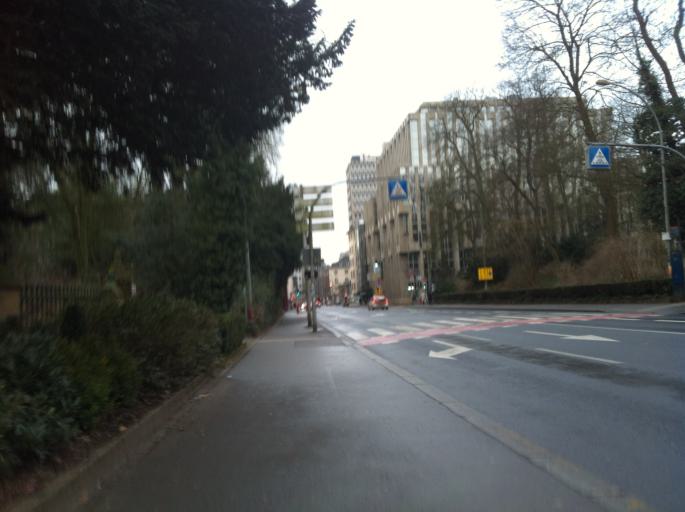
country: LU
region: Luxembourg
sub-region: Canton de Luxembourg
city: Luxembourg
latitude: 49.6154
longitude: 6.1270
